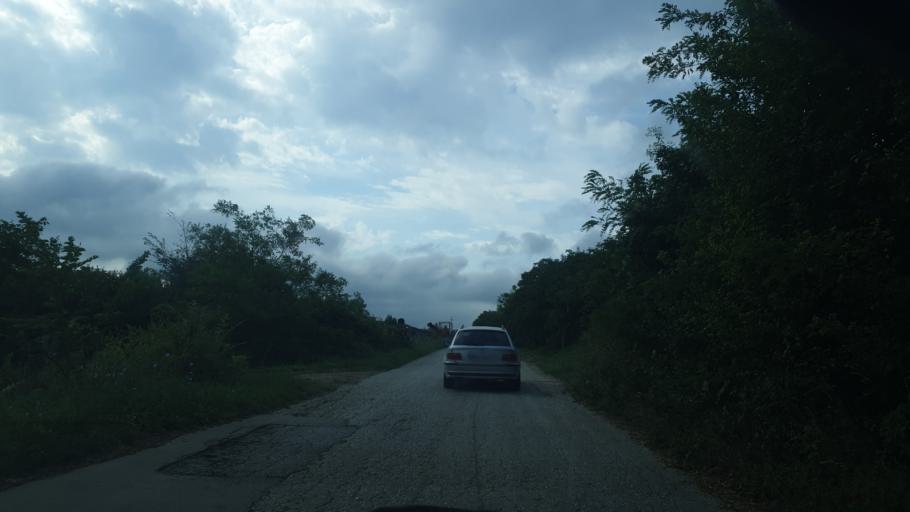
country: RS
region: Central Serbia
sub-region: Sumadijski Okrug
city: Kragujevac
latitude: 44.1007
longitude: 20.7805
